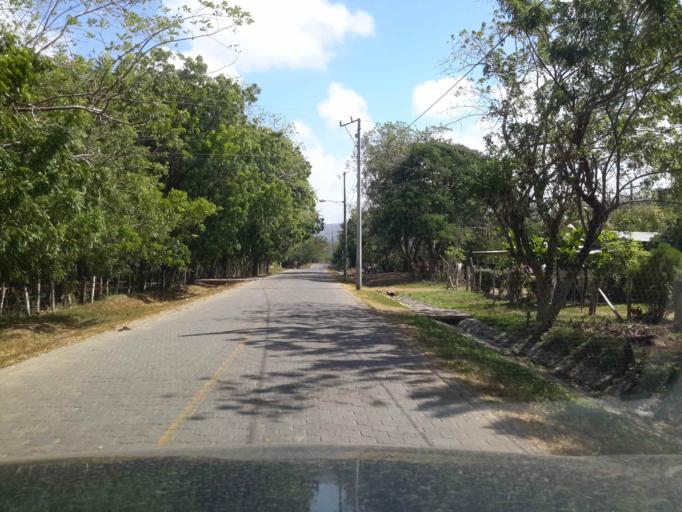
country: NI
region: Rivas
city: San Juan del Sur
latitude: 11.2446
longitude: -85.8437
